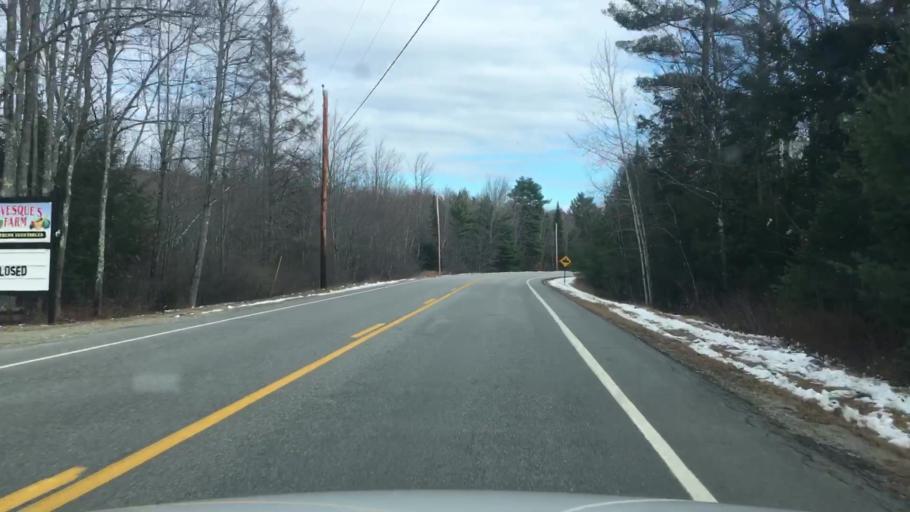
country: US
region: Maine
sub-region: Androscoggin County
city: Leeds
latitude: 44.3487
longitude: -70.1181
